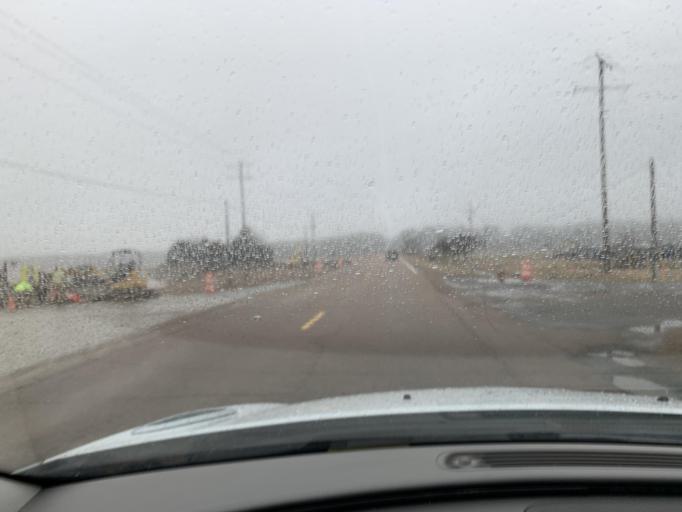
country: US
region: Mississippi
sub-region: De Soto County
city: Hernando
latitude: 34.8670
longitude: -89.9954
